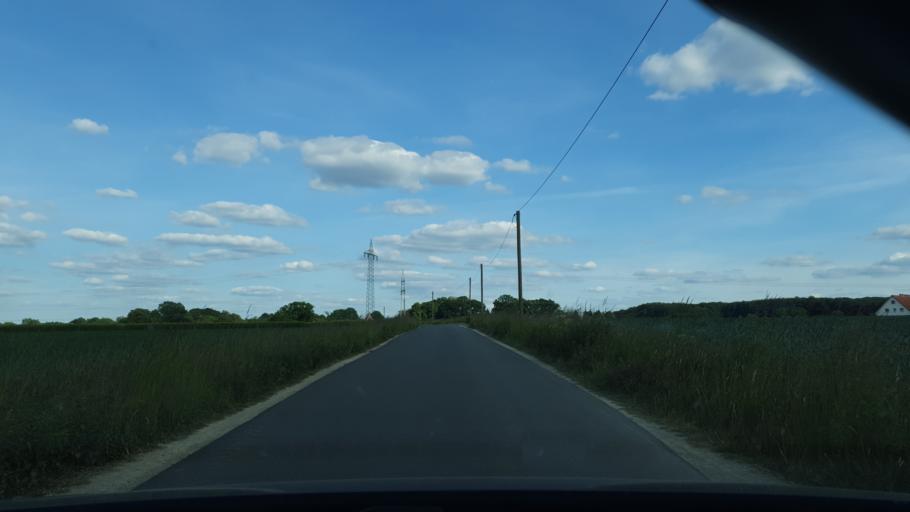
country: DE
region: North Rhine-Westphalia
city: Enger
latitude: 52.1670
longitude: 8.5367
